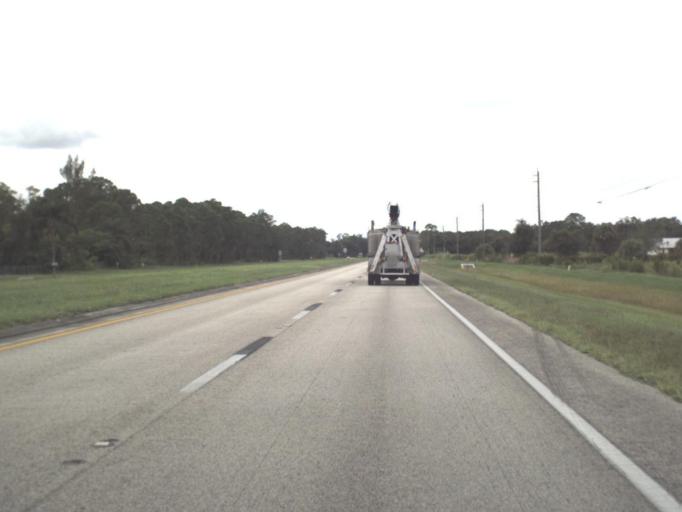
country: US
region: Florida
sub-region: Lee County
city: Alva
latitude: 26.7135
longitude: -81.6590
